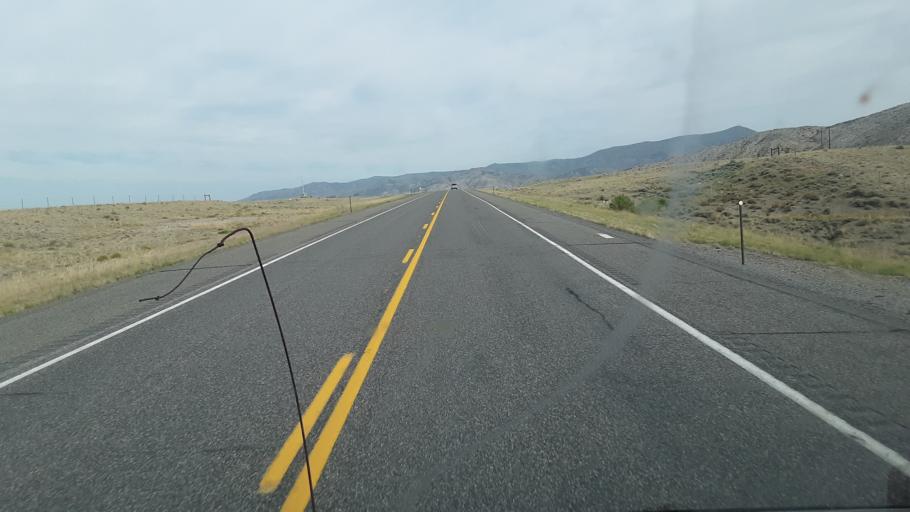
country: US
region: Wyoming
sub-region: Hot Springs County
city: Thermopolis
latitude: 43.3801
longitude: -108.1374
